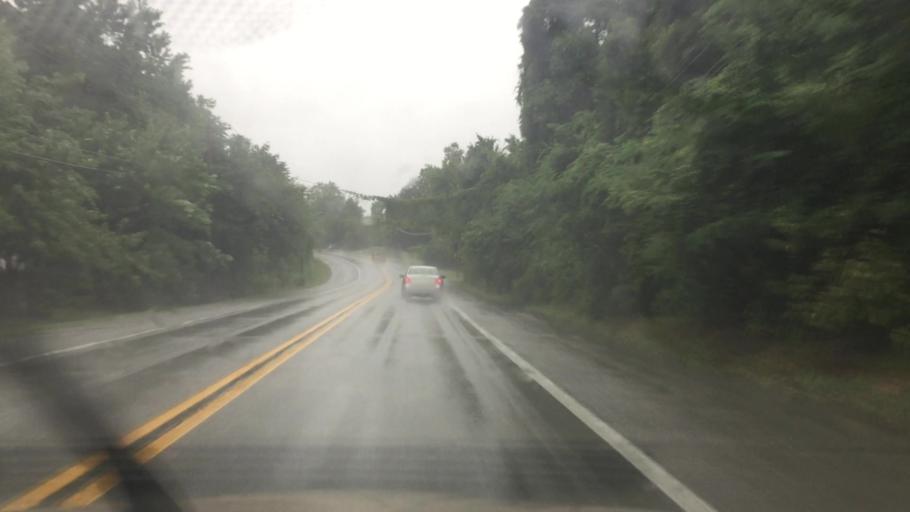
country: US
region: Maryland
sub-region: Anne Arundel County
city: Fort Meade
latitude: 39.1385
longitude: -76.7332
